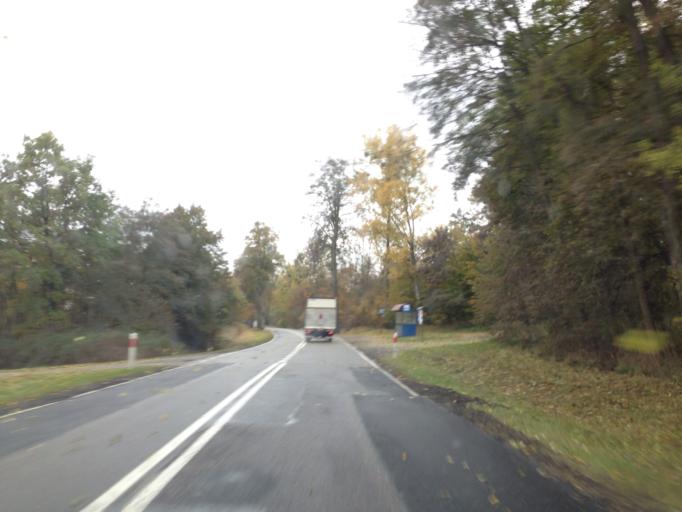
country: PL
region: Pomeranian Voivodeship
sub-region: Powiat kwidzynski
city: Ryjewo
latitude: 53.8539
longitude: 19.0000
